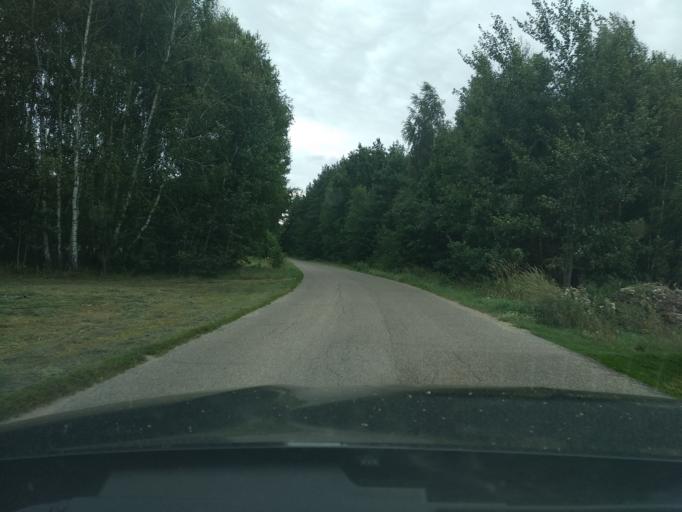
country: PL
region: Masovian Voivodeship
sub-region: Powiat pultuski
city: Obryte
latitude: 52.7435
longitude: 21.2151
